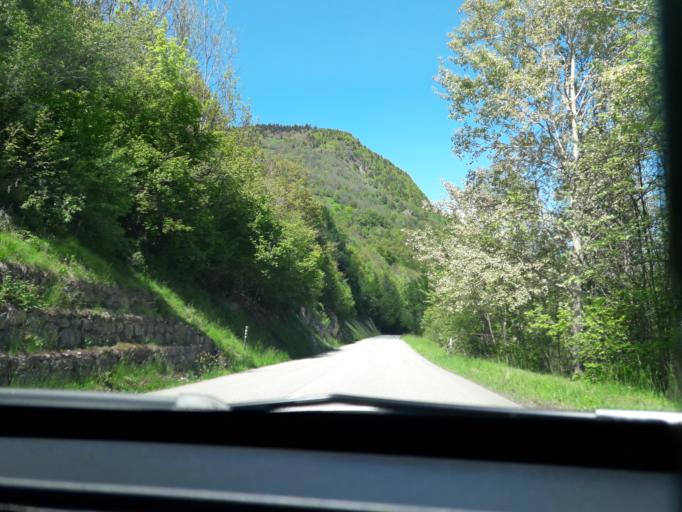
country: FR
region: Rhone-Alpes
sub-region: Departement de la Savoie
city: Salins-les-Thermes
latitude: 45.4459
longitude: 6.4958
